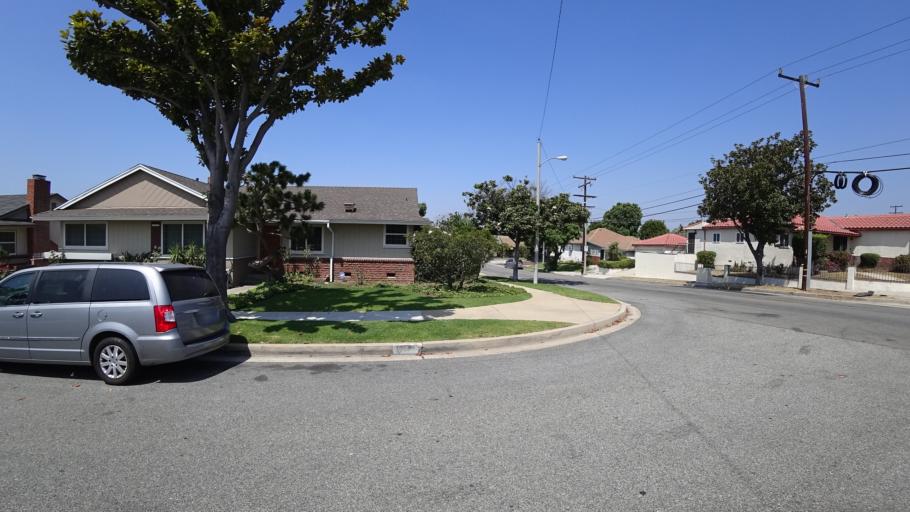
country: US
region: California
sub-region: Los Angeles County
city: Westmont
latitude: 33.9417
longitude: -118.3187
